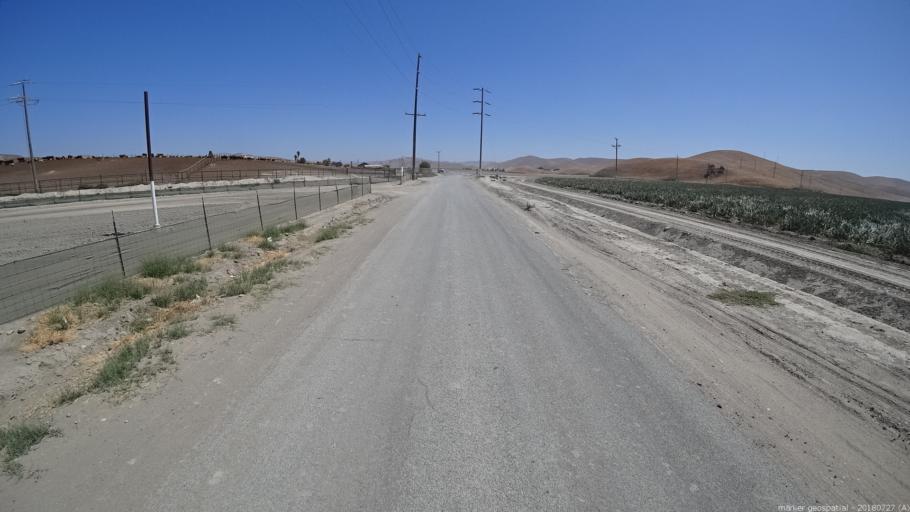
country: US
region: California
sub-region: Monterey County
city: King City
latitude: 36.0747
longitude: -120.9318
